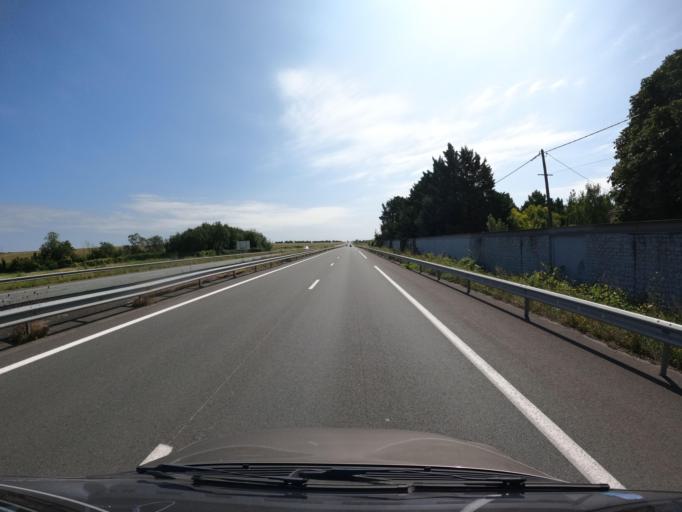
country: FR
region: Poitou-Charentes
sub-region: Departement des Deux-Sevres
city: Mauze-sur-le-Mignon
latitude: 46.2022
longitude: -0.7158
